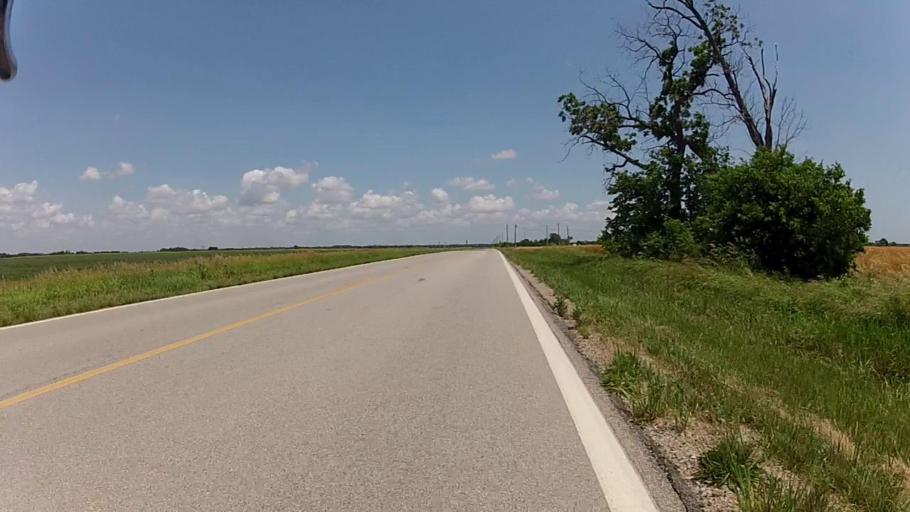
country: US
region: Kansas
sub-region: Labette County
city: Altamont
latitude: 37.1925
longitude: -95.4335
